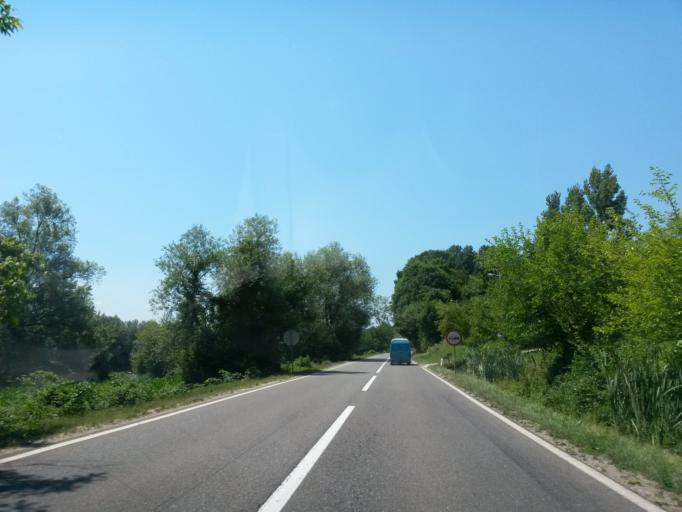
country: BA
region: Federation of Bosnia and Herzegovina
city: Odzak
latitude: 44.9611
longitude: 18.2224
